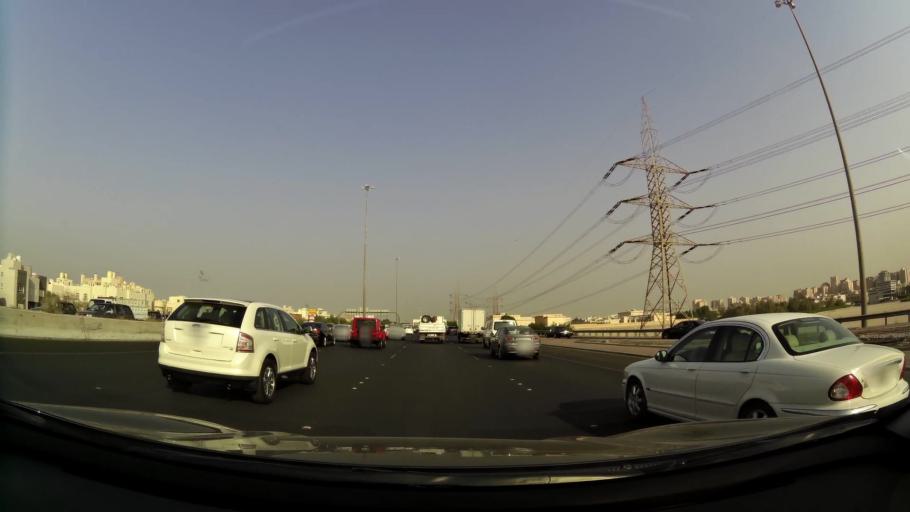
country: KW
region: Al Farwaniyah
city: Al Farwaniyah
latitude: 29.3030
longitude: 47.9663
